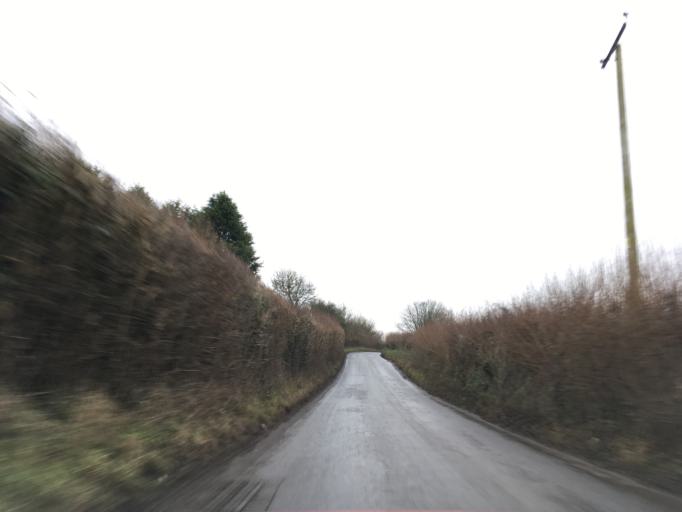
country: GB
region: England
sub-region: Gloucestershire
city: Wotton-under-Edge
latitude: 51.6130
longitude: -2.3346
